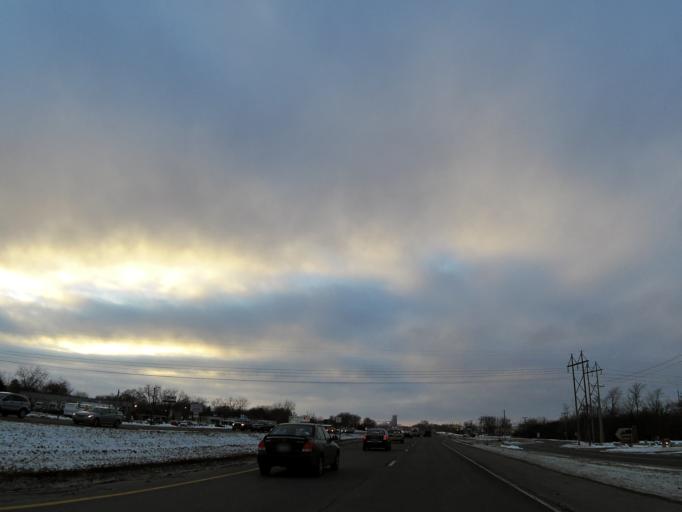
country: US
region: Minnesota
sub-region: Scott County
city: Savage
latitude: 44.7770
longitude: -93.3231
